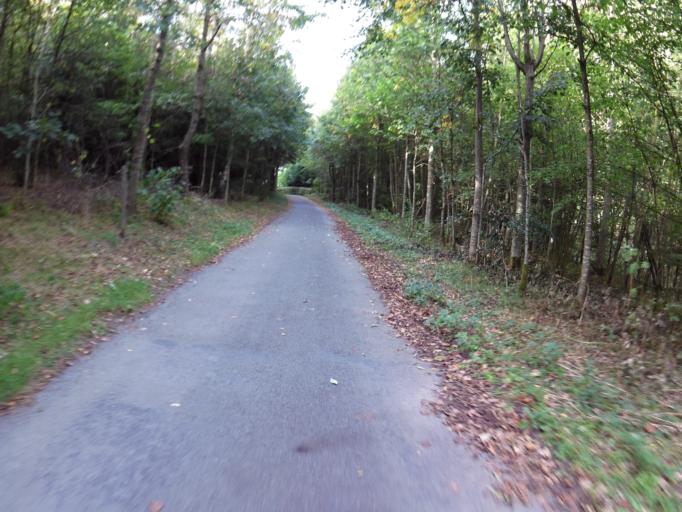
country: BE
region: Wallonia
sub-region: Province de Liege
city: Saint-Vith
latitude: 50.2624
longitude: 6.1460
